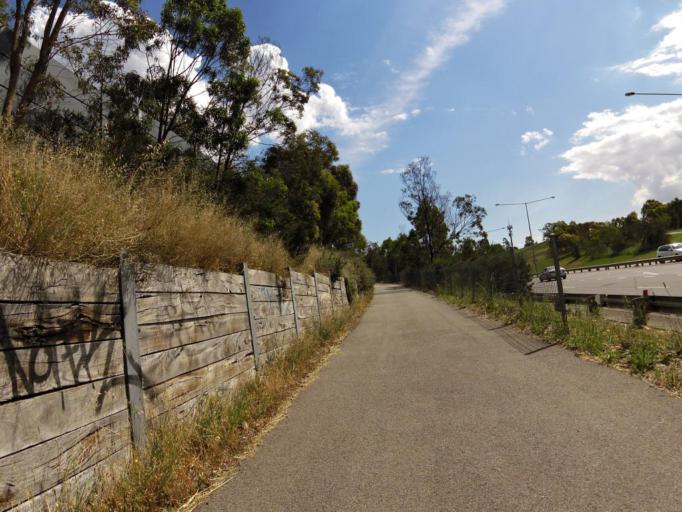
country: AU
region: Victoria
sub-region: Banyule
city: Greensborough
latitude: -37.6927
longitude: 145.0973
